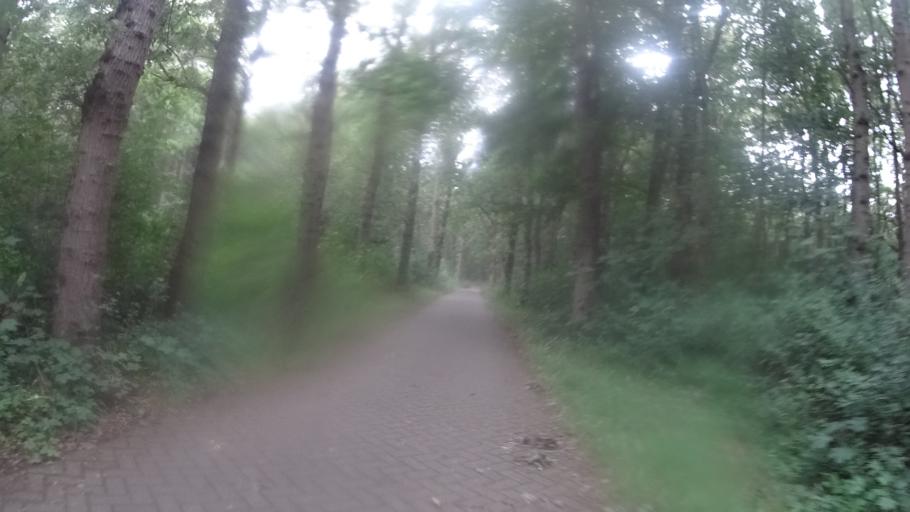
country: NL
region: North Holland
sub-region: Gemeente Castricum
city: Castricum
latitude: 52.5523
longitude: 4.6424
